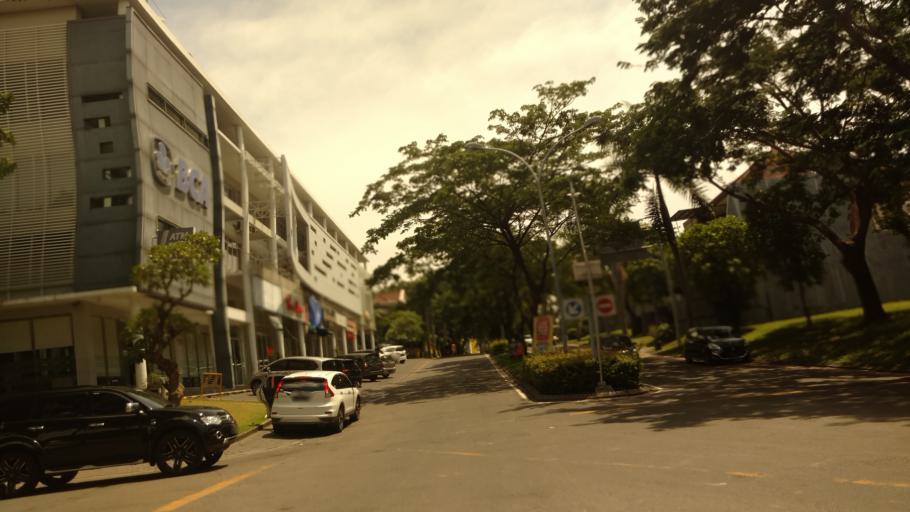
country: ID
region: East Java
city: Driyorejo
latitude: -7.2942
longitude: 112.6545
